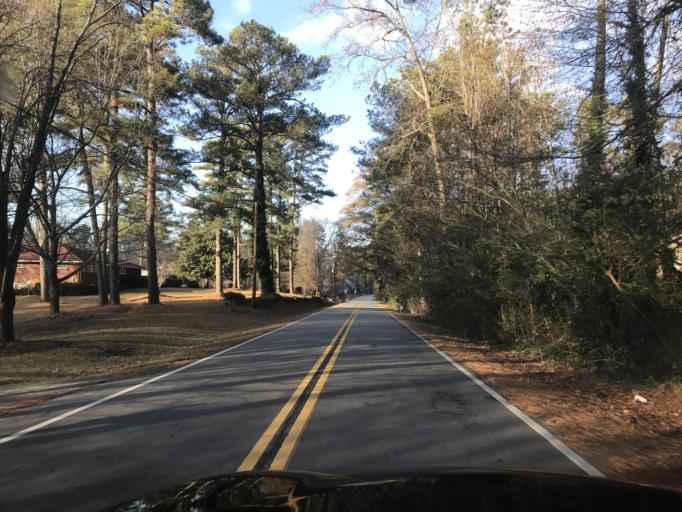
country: US
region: Georgia
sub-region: Fulton County
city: College Park
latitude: 33.6297
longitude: -84.4874
